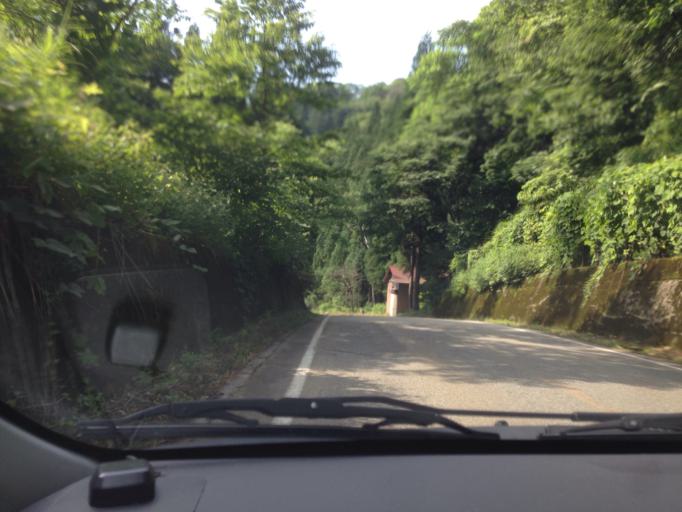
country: JP
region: Fukushima
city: Kitakata
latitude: 37.4303
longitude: 139.5393
